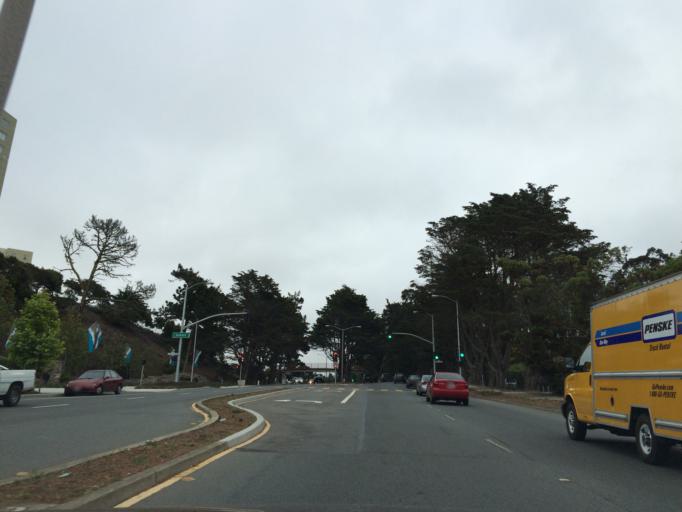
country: US
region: California
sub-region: San Mateo County
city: Daly City
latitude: 37.7140
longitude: -122.4752
